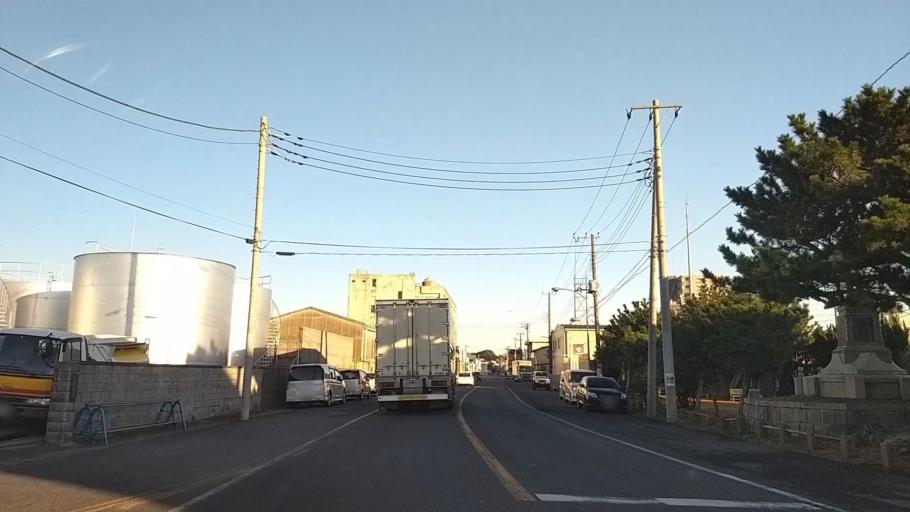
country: JP
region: Chiba
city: Hasaki
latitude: 35.7345
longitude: 140.8346
